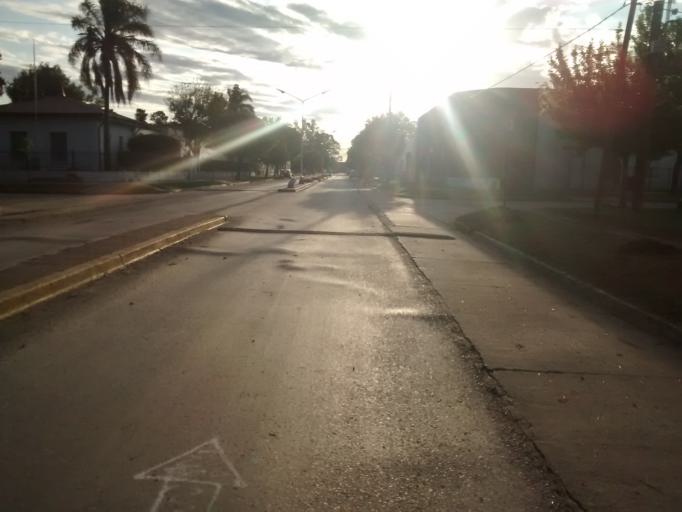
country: AR
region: Santa Fe
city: Galvez
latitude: -31.9040
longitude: -61.2758
